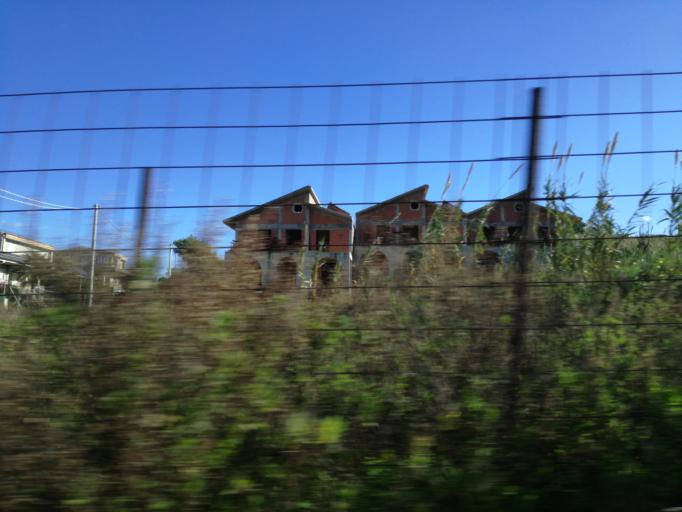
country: IT
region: Sicily
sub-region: Provincia di Caltanissetta
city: Gela
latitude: 37.0924
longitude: 14.1771
